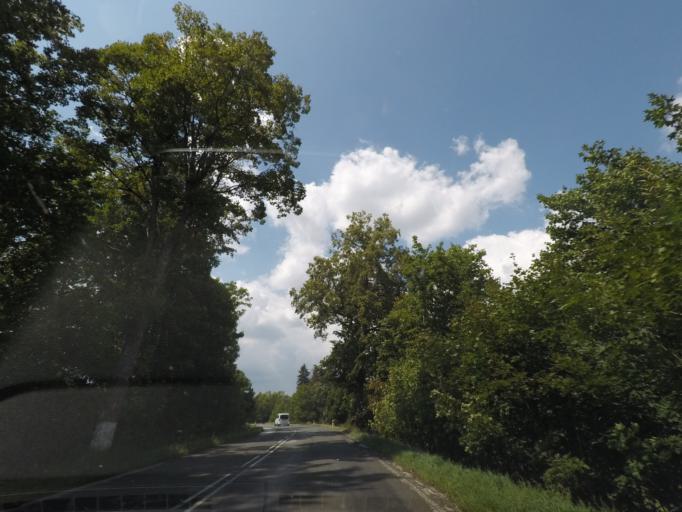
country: CZ
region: Kralovehradecky
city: Zadni Mostek
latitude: 50.5373
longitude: 15.6675
